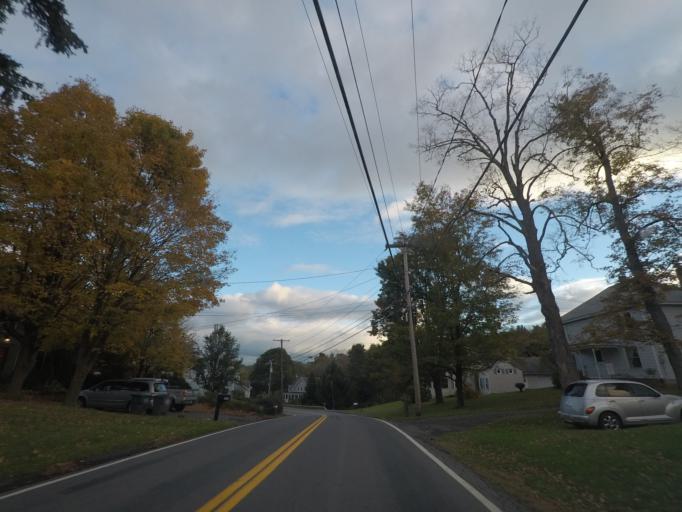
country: US
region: New York
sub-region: Rensselaer County
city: Nassau
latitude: 42.5611
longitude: -73.6334
